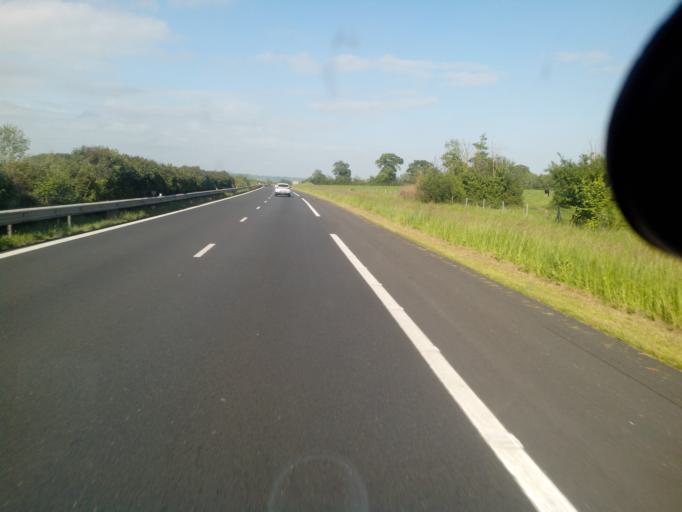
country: FR
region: Lower Normandy
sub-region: Departement du Calvados
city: Bavent
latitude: 49.2133
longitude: -0.1368
